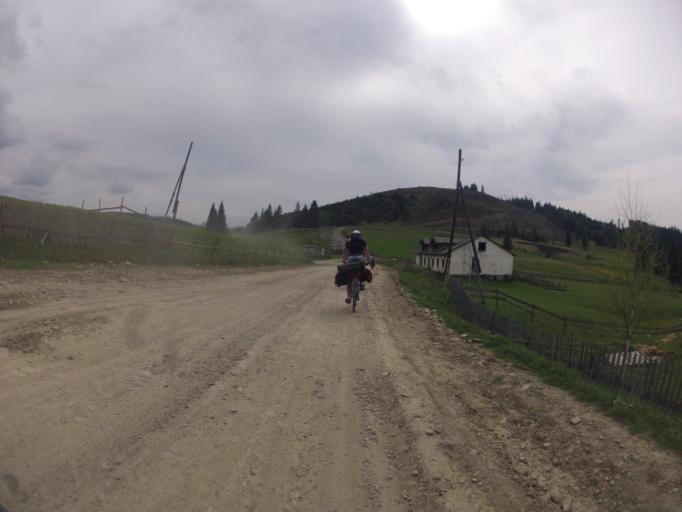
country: UA
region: Chernivtsi
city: Putyla
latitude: 47.8893
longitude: 25.1656
